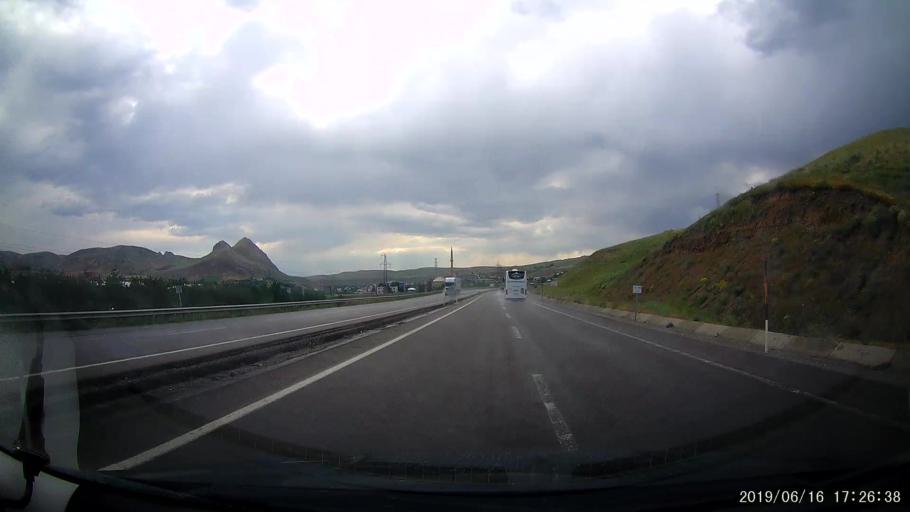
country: TR
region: Erzincan
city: Tercan
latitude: 39.7697
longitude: 40.4081
